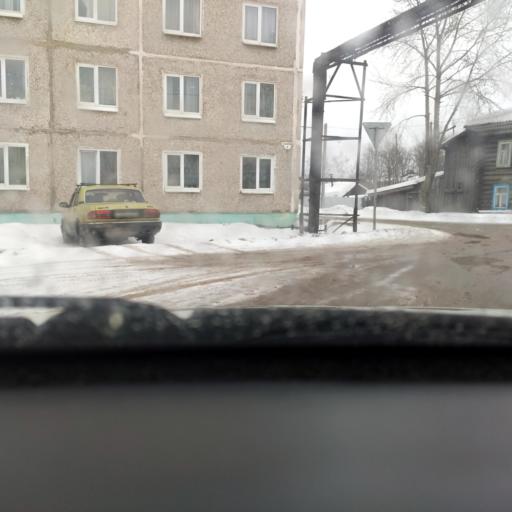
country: RU
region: Perm
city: Yugo-Kamskiy
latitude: 57.7067
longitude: 55.5991
